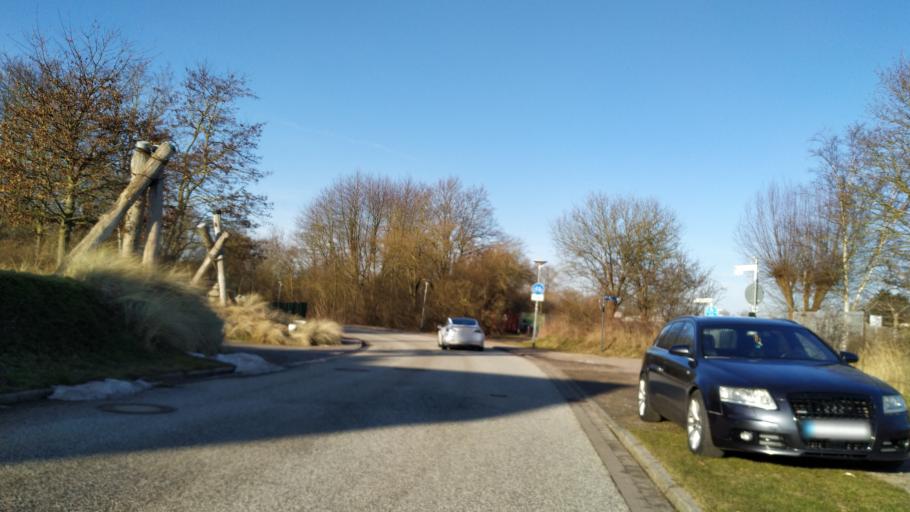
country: DE
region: Schleswig-Holstein
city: Neustadt in Holstein
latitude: 54.0990
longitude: 10.7997
